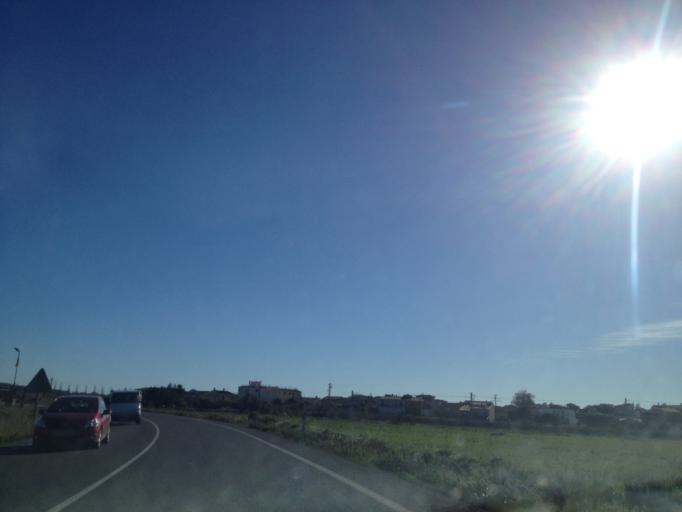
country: ES
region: Balearic Islands
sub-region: Illes Balears
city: Petra
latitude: 39.6204
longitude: 3.1115
